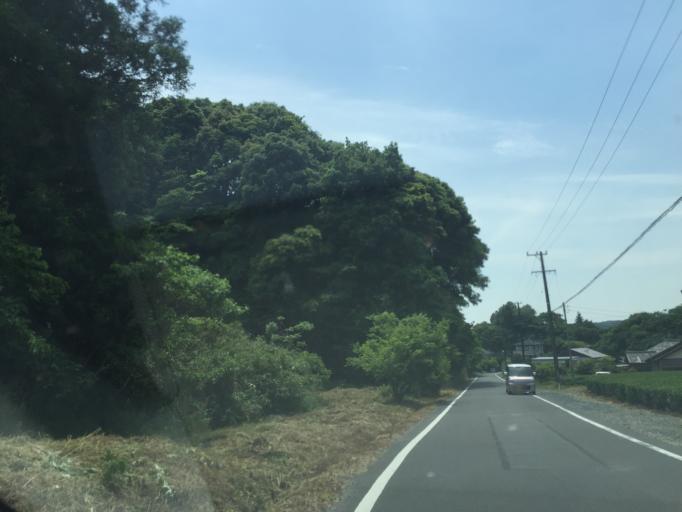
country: JP
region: Shizuoka
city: Mori
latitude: 34.7949
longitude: 137.9669
